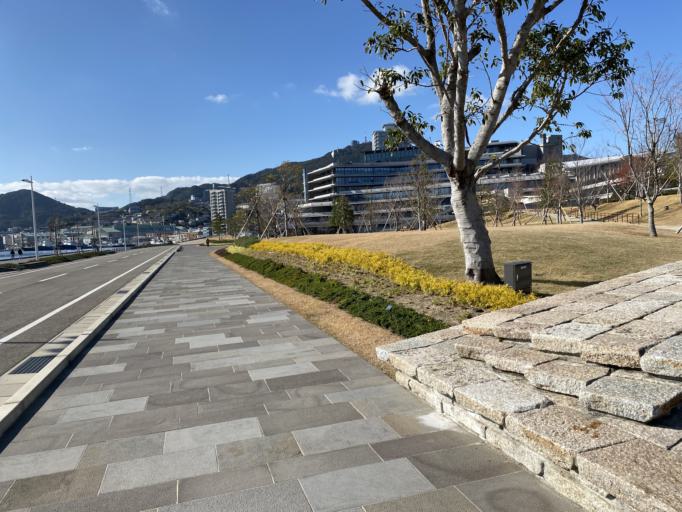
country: JP
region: Nagasaki
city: Nagasaki-shi
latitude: 32.7492
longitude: 129.8699
